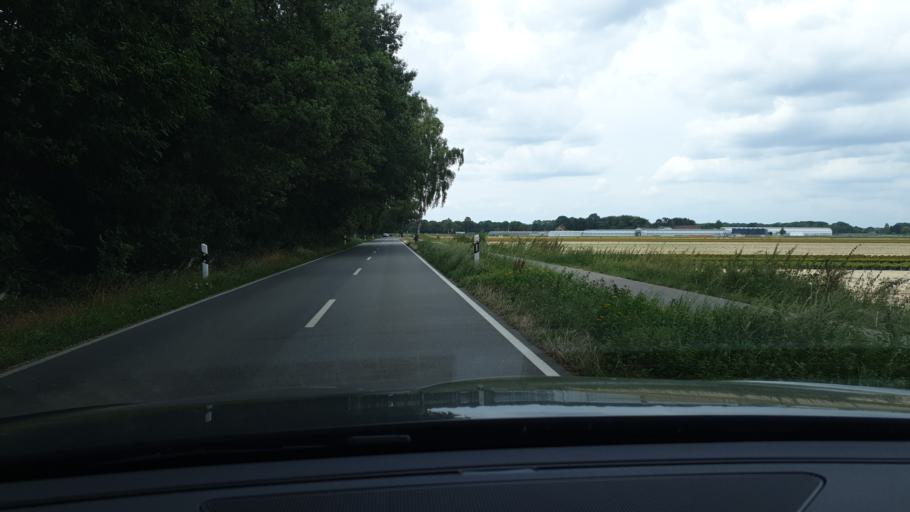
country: NL
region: Limburg
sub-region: Gemeente Venlo
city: Arcen
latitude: 51.4801
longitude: 6.2214
